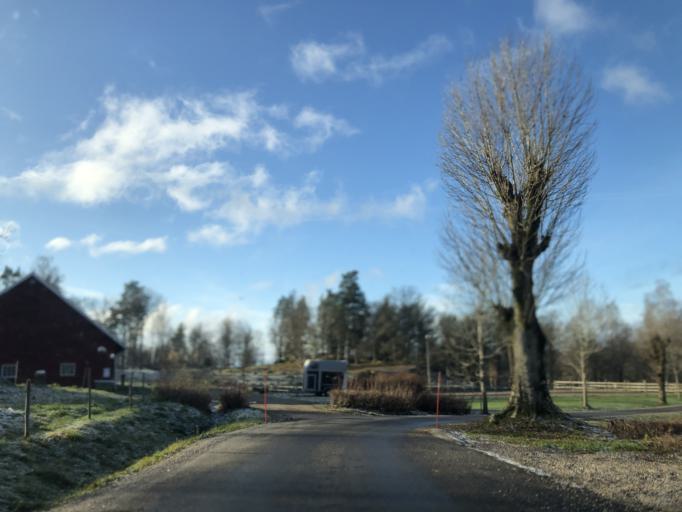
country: SE
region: Vaestra Goetaland
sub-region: Ulricehamns Kommun
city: Ulricehamn
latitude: 57.7252
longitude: 13.4129
